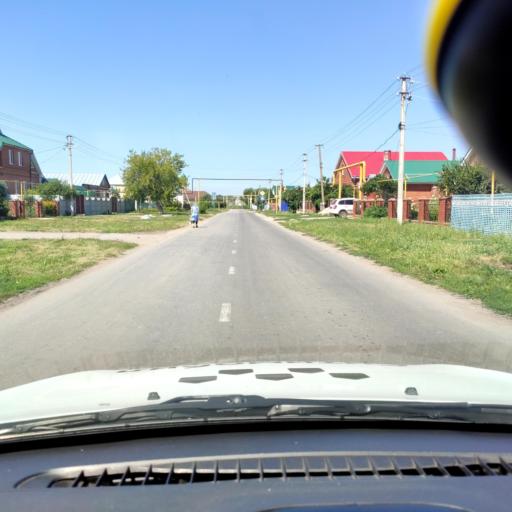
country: RU
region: Samara
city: Tol'yatti
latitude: 53.6379
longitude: 49.2939
